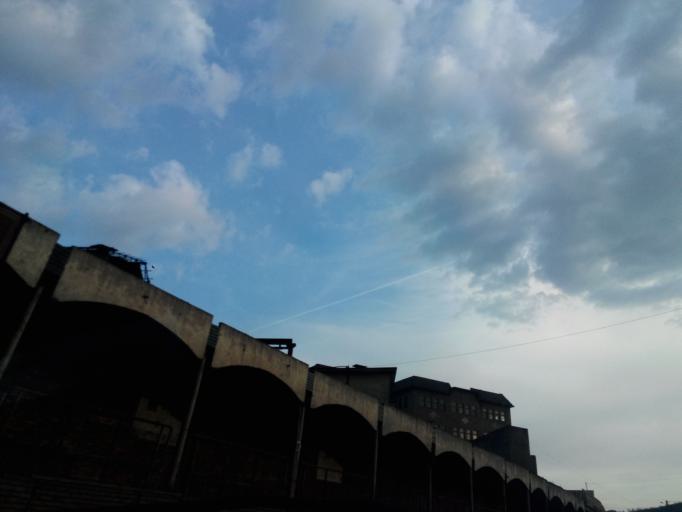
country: RO
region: Prahova
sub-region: Comuna Comarnic
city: Ghiosesti
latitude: 45.2361
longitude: 25.6370
